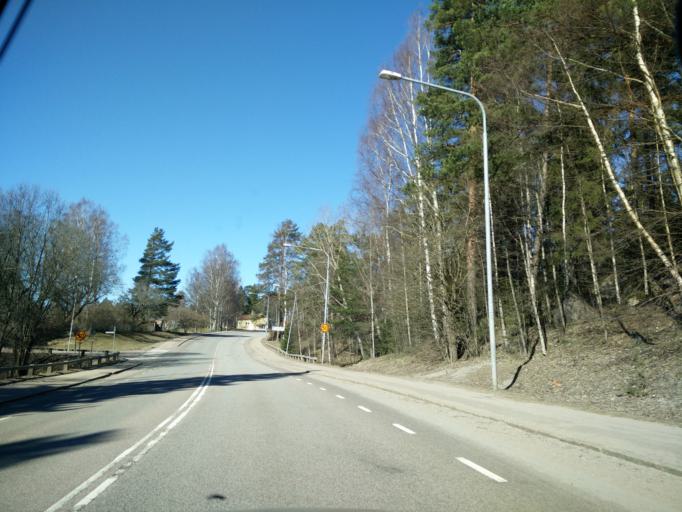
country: SE
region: Vaermland
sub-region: Hagfors Kommun
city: Hagfors
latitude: 60.0259
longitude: 13.6998
